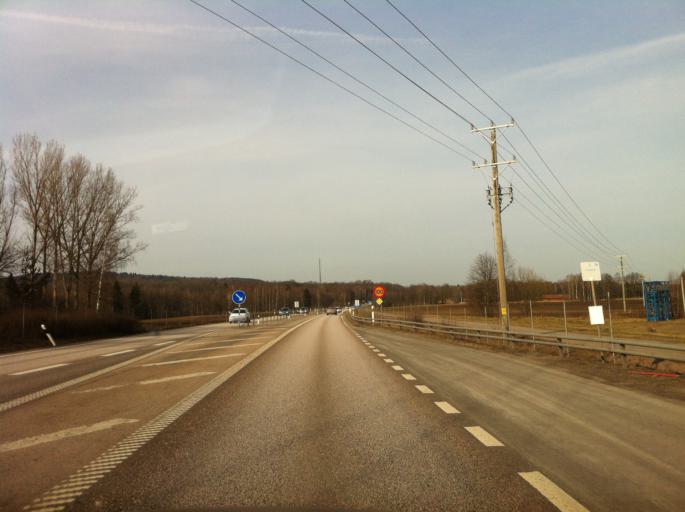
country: SE
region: Vaestra Goetaland
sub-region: Skovde Kommun
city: Stopen
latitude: 58.4440
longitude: 13.8528
